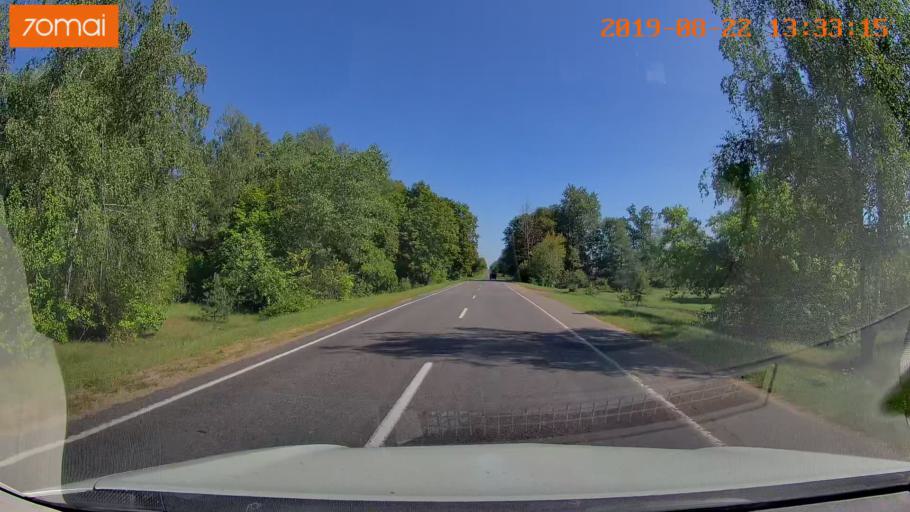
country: BY
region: Minsk
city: Staryya Darohi
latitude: 53.2166
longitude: 28.2206
